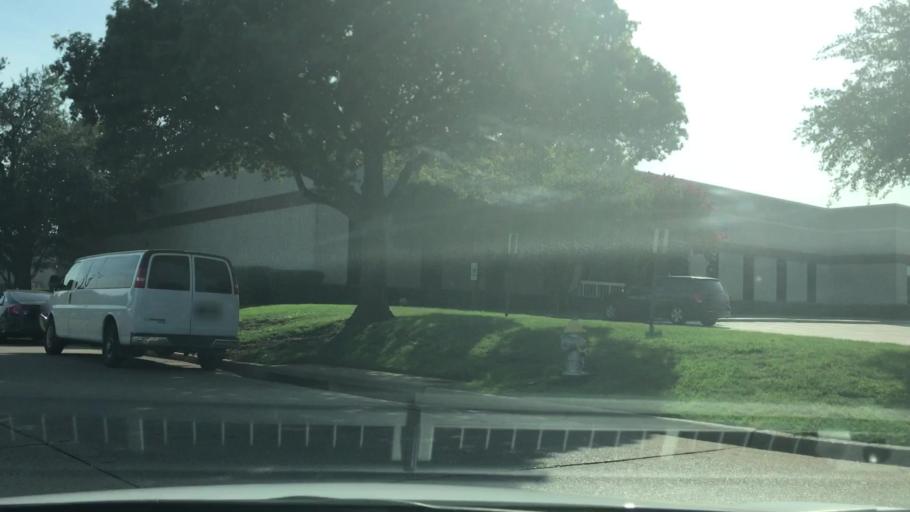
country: US
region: Texas
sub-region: Dallas County
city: Richardson
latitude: 32.8914
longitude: -96.7038
